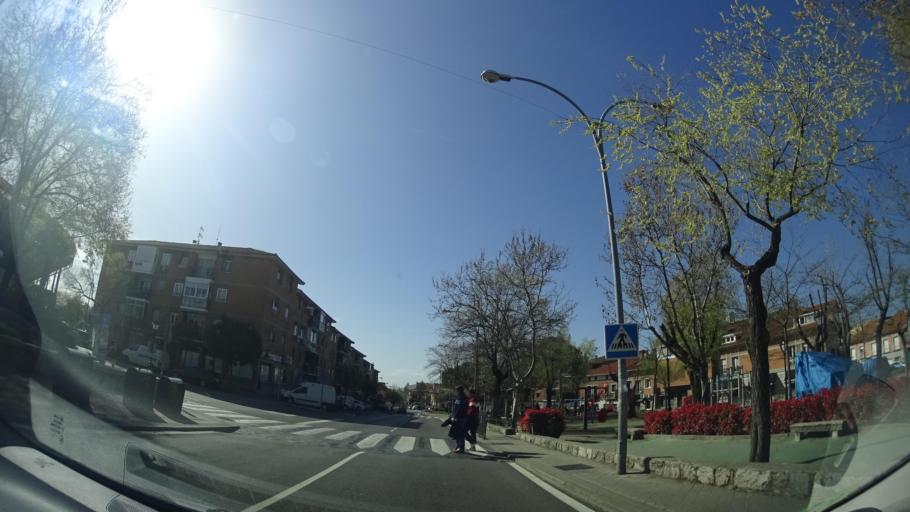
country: ES
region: Madrid
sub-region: Provincia de Madrid
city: Colmenar Viejo
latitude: 40.6662
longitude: -3.7697
